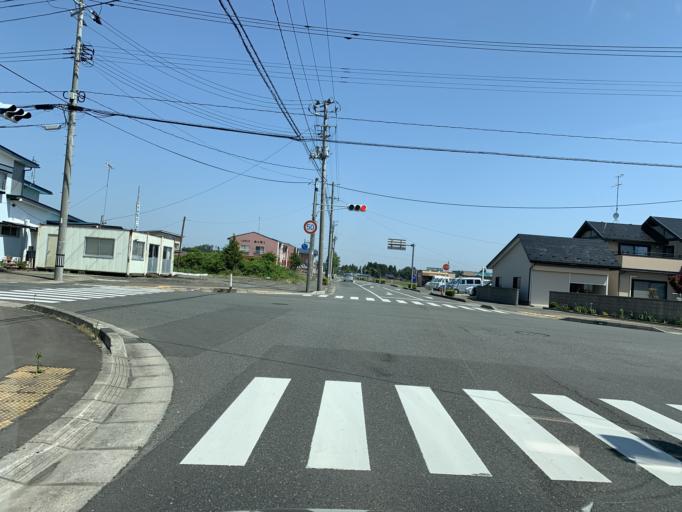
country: JP
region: Iwate
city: Mizusawa
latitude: 39.1959
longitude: 141.0952
